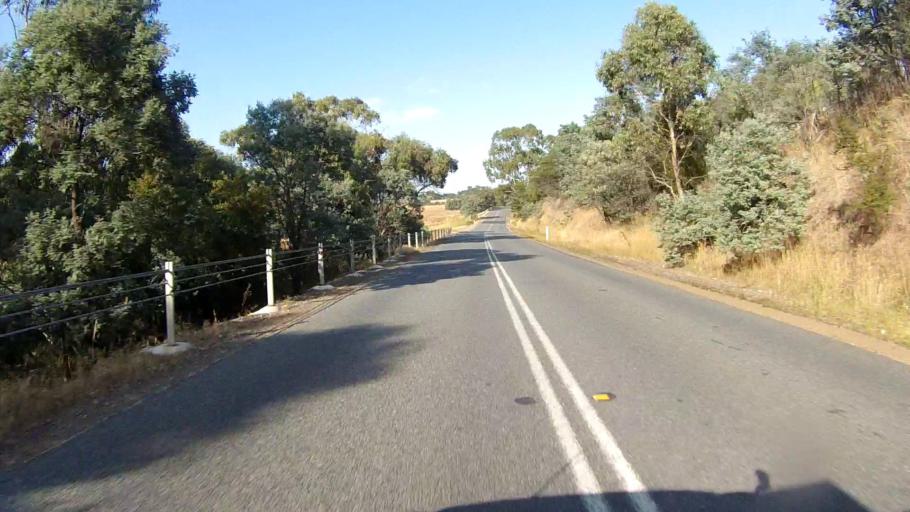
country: AU
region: Tasmania
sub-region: Derwent Valley
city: New Norfolk
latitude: -42.7594
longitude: 147.1386
